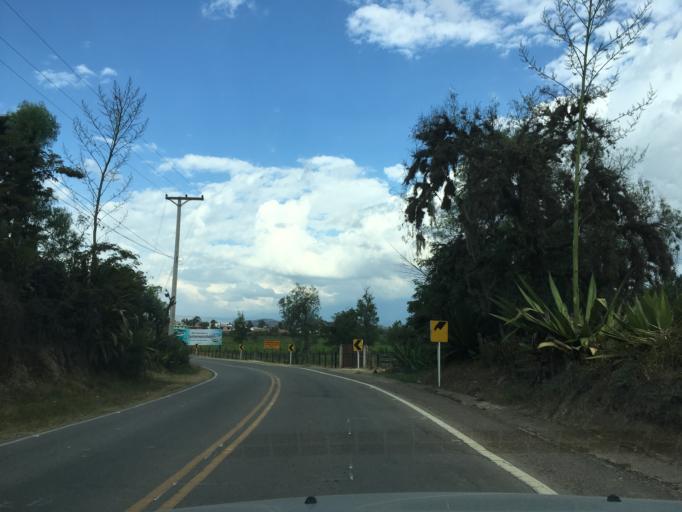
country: CO
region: Boyaca
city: Sutamarchan
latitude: 5.6129
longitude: -73.6253
